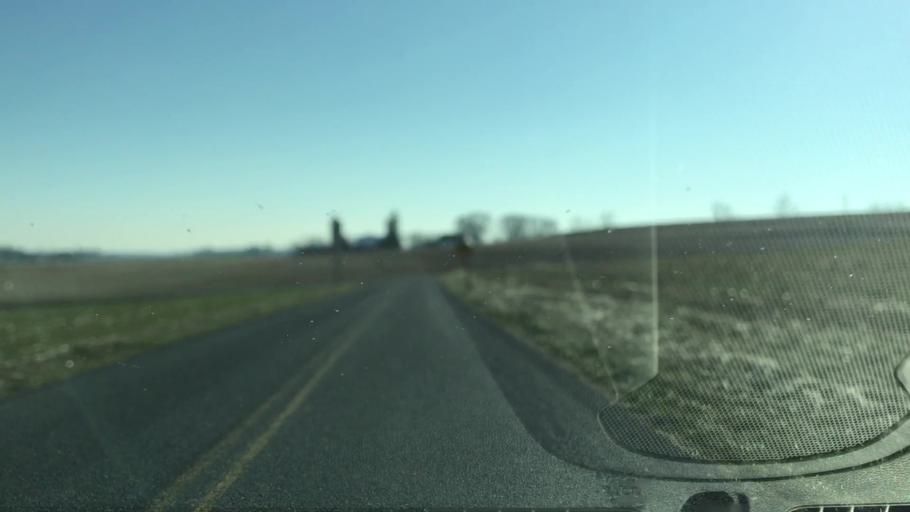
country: US
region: Pennsylvania
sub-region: Lancaster County
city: Maytown
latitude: 40.0973
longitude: -76.6138
